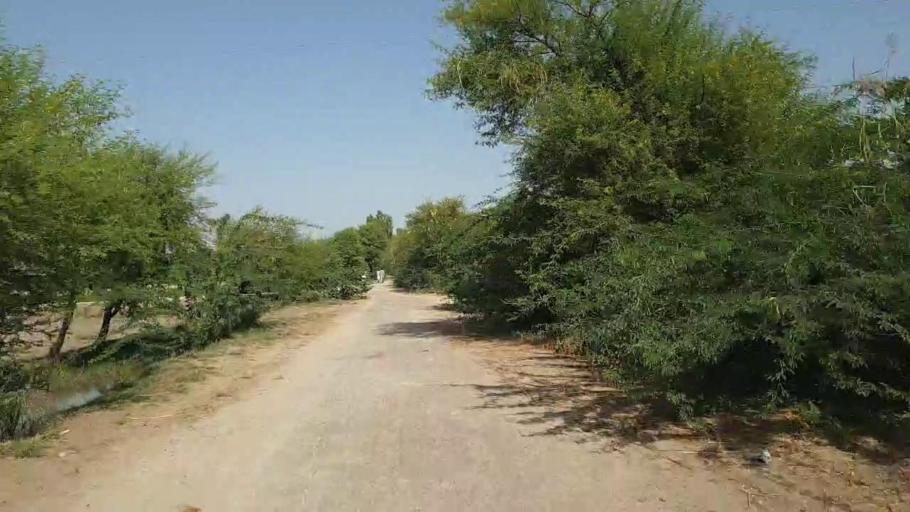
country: PK
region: Sindh
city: Tando Bago
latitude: 24.7663
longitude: 69.0231
